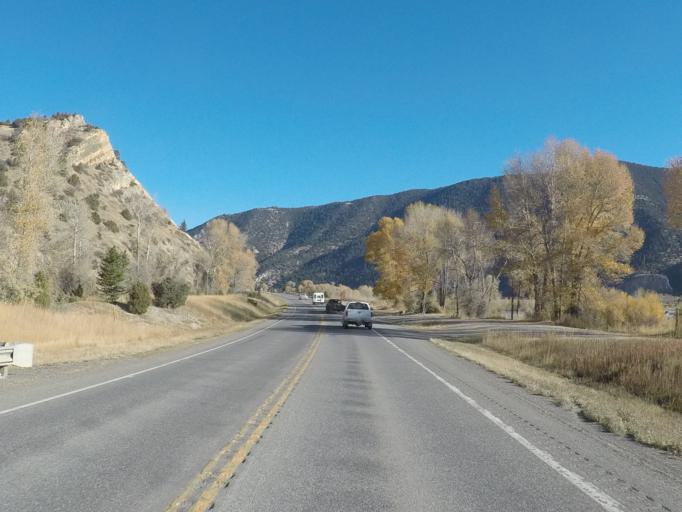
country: US
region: Montana
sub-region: Park County
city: Livingston
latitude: 45.5841
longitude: -110.5755
